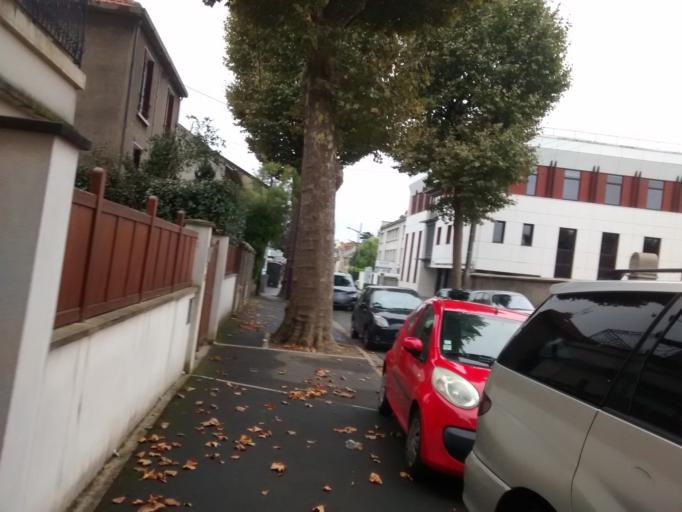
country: FR
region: Ile-de-France
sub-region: Departement du Val-de-Marne
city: L'Hay-les-Roses
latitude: 48.7809
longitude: 2.3394
